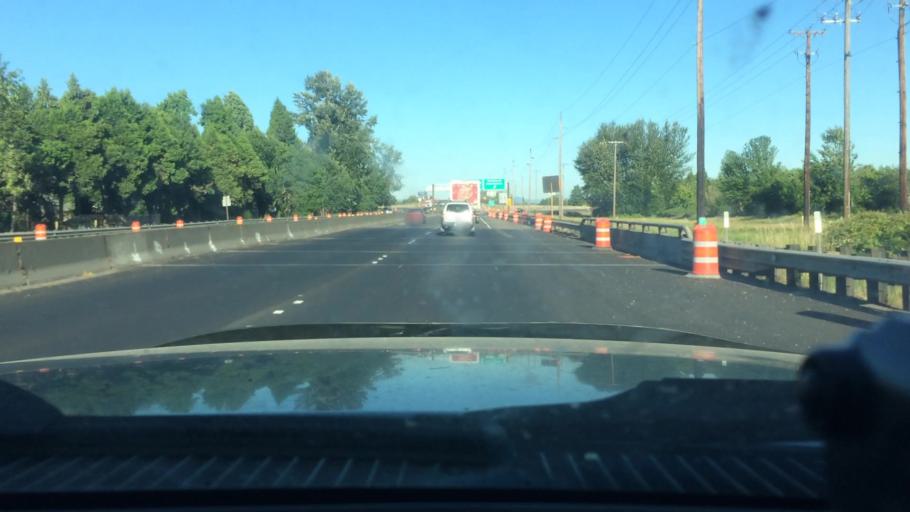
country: US
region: Oregon
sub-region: Lane County
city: Eugene
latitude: 44.0980
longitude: -123.1482
